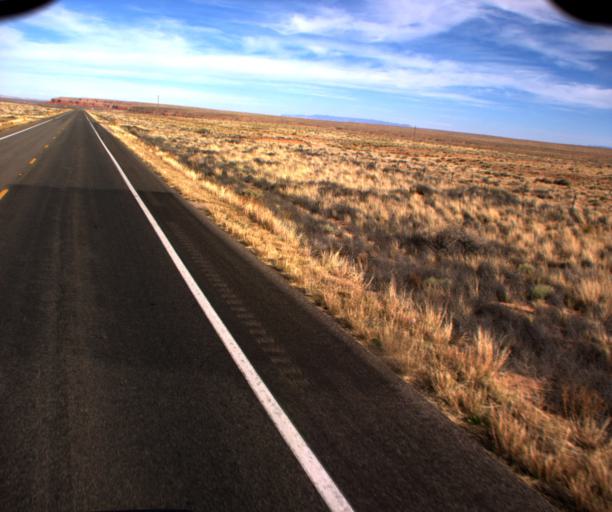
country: US
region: Arizona
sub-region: Navajo County
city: Kayenta
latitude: 36.7374
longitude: -110.0882
